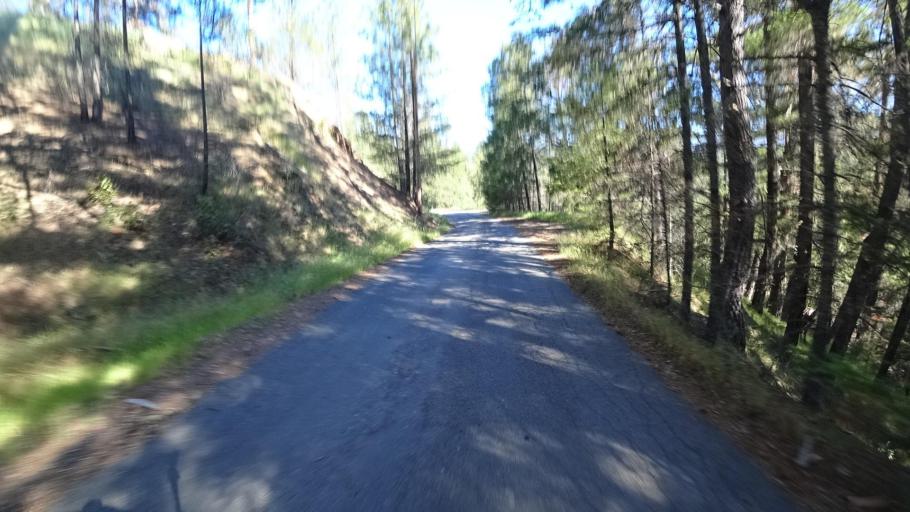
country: US
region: California
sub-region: Lake County
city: Upper Lake
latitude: 39.4057
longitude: -122.9723
